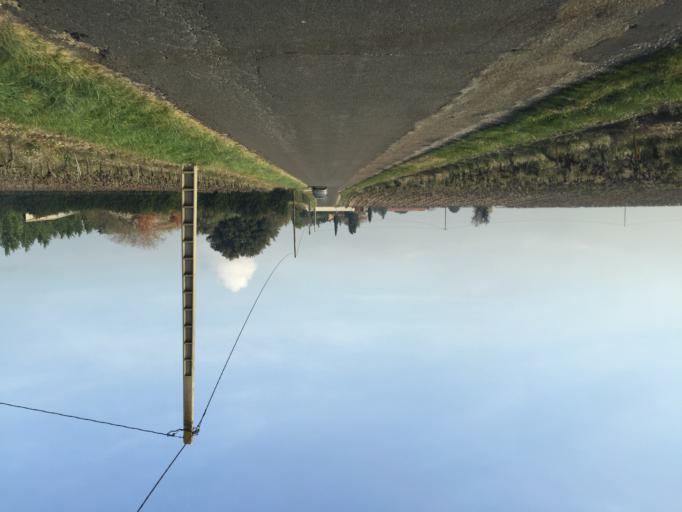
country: FR
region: Provence-Alpes-Cote d'Azur
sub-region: Departement du Vaucluse
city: Jonquieres
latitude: 44.1267
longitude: 4.8786
